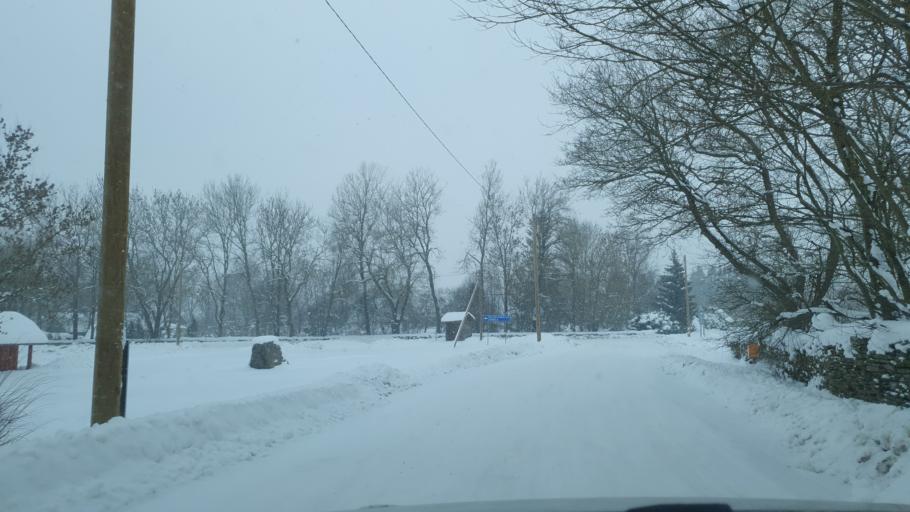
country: EE
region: Harju
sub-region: Maardu linn
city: Maardu
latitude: 59.4591
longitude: 25.0893
